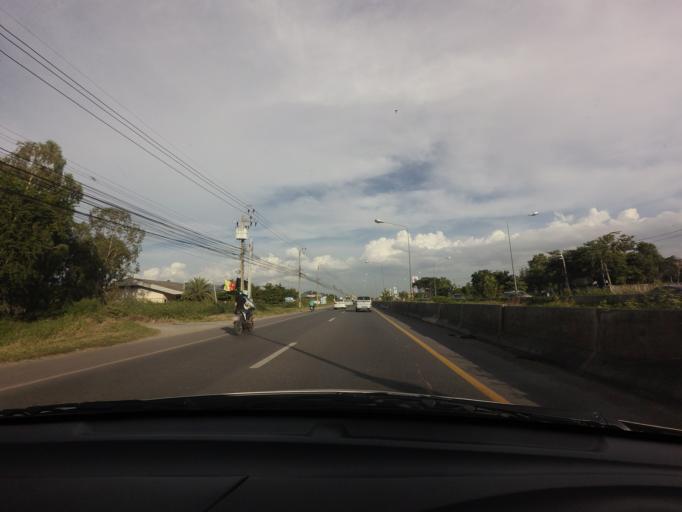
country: TH
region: Nonthaburi
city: Bang Bua Thong
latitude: 13.9606
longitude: 100.4031
